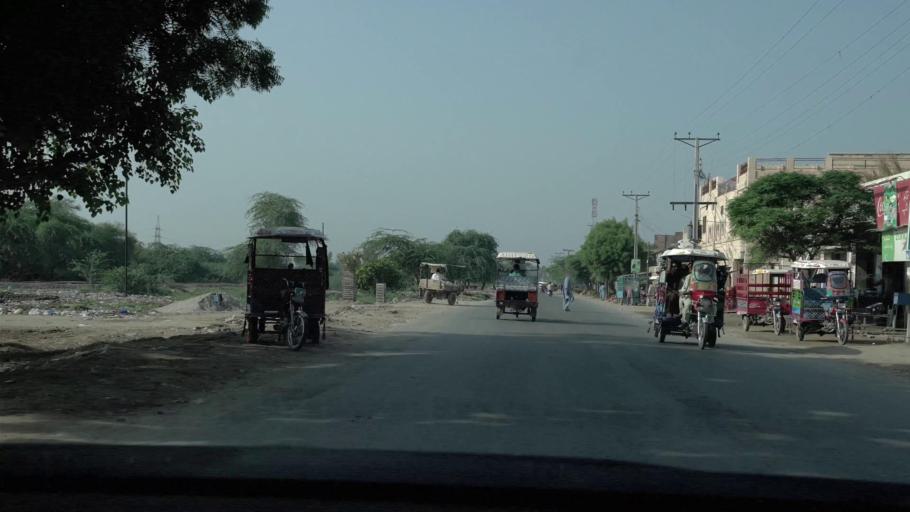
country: PK
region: Punjab
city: Gojra
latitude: 31.1232
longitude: 72.6708
